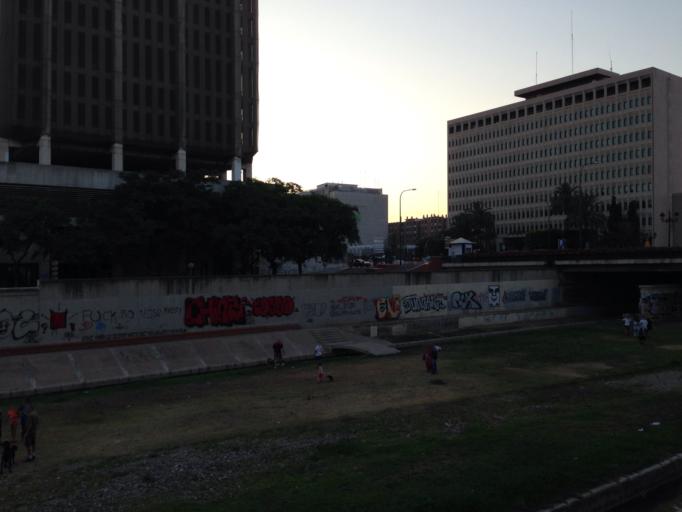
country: ES
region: Andalusia
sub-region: Provincia de Malaga
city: Malaga
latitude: 36.7160
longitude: -4.4257
